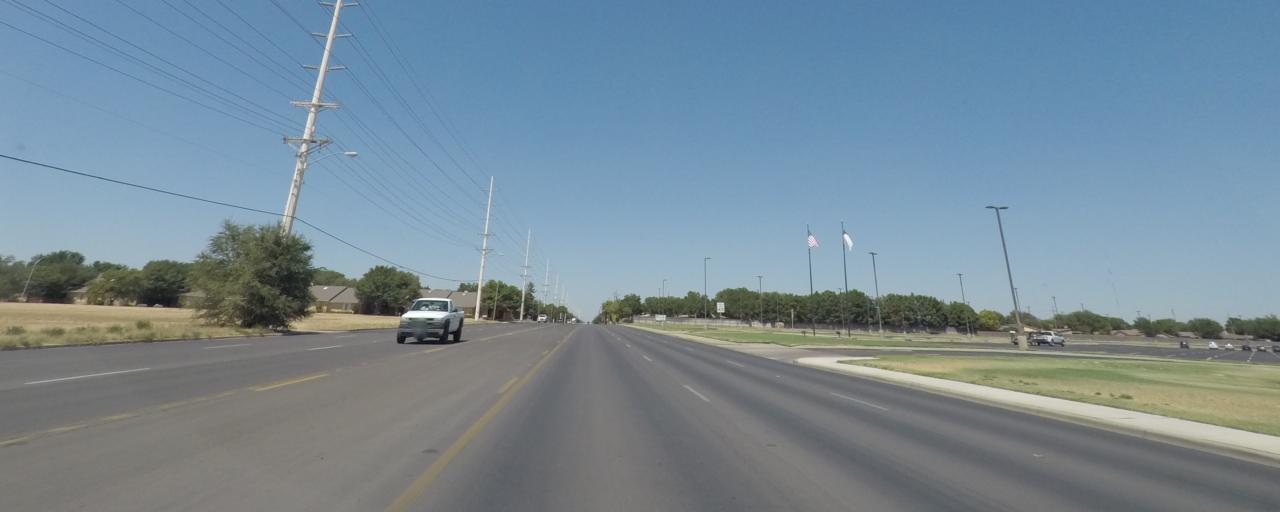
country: US
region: Texas
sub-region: Lubbock County
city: Lubbock
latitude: 33.5065
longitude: -101.8875
